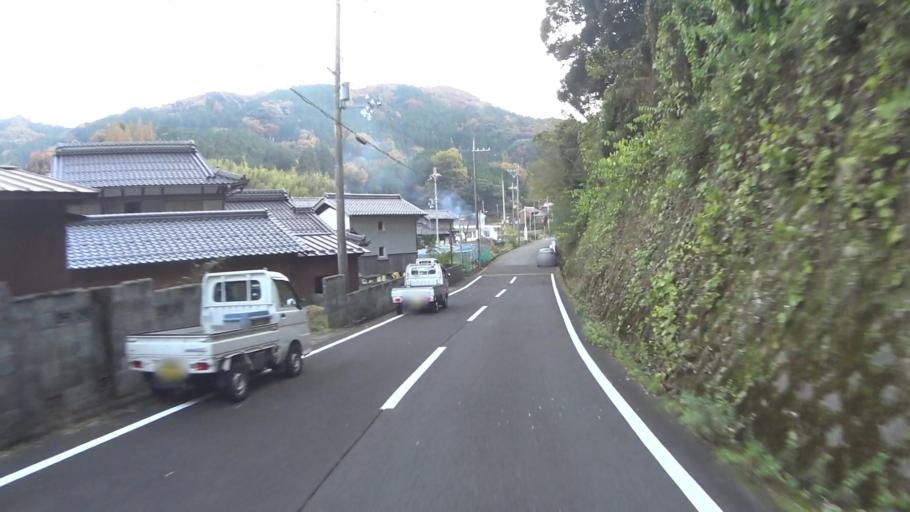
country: JP
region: Kyoto
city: Maizuru
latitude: 35.5660
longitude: 135.4524
